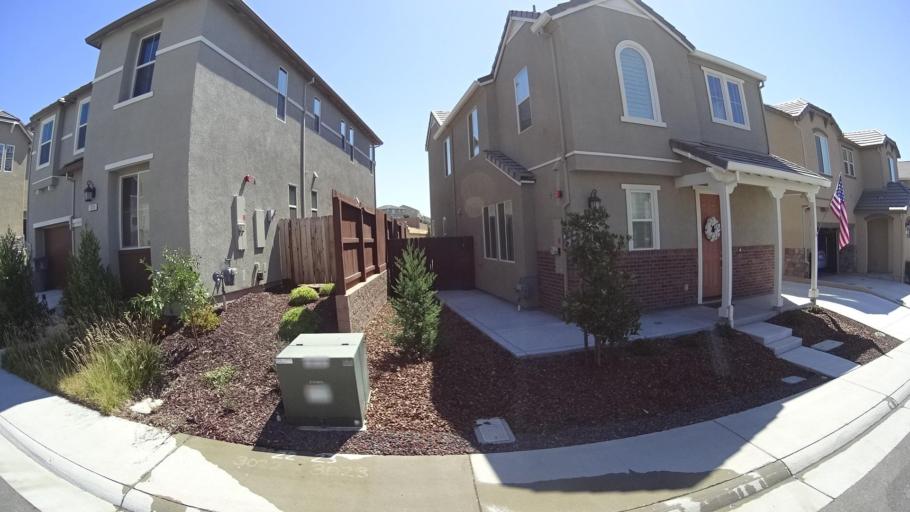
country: US
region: California
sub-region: Placer County
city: Lincoln
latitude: 38.8270
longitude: -121.2925
